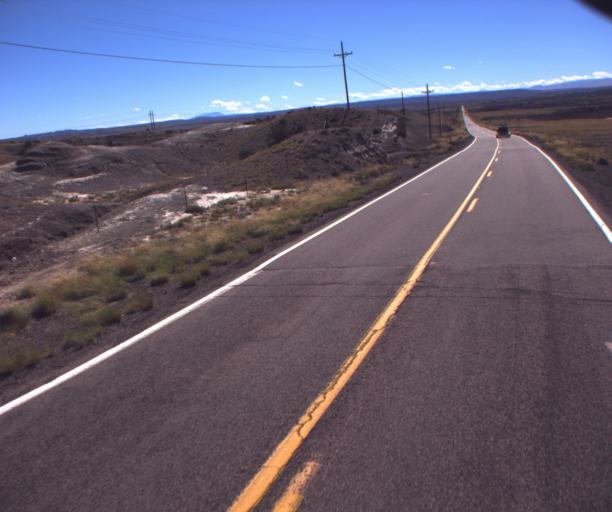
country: US
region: Arizona
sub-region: Apache County
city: Saint Johns
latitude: 34.5592
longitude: -109.3422
